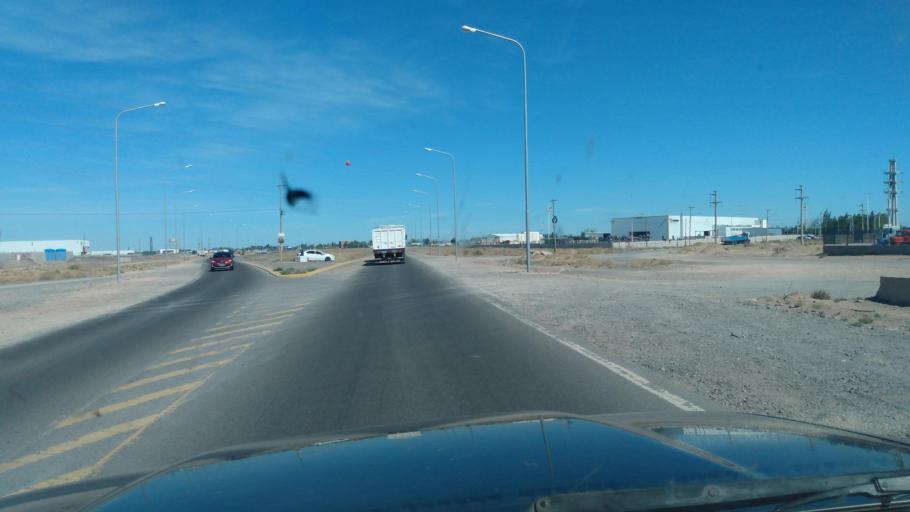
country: AR
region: Neuquen
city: Neuquen
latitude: -38.9139
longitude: -68.1132
